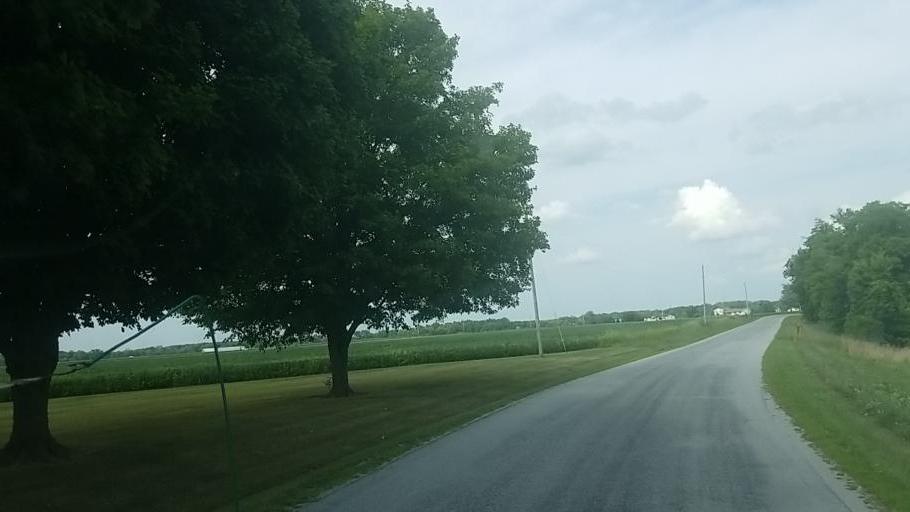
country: US
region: Ohio
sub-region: Wyandot County
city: Upper Sandusky
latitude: 40.8201
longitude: -83.3656
